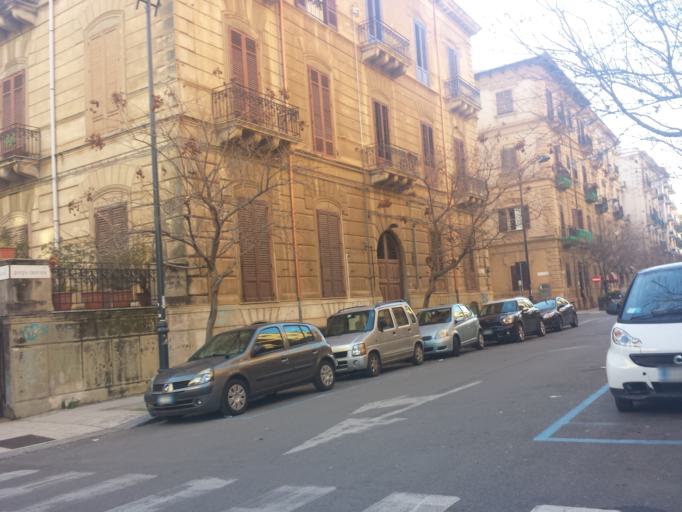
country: IT
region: Sicily
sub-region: Palermo
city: Palermo
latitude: 38.1306
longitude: 13.3538
